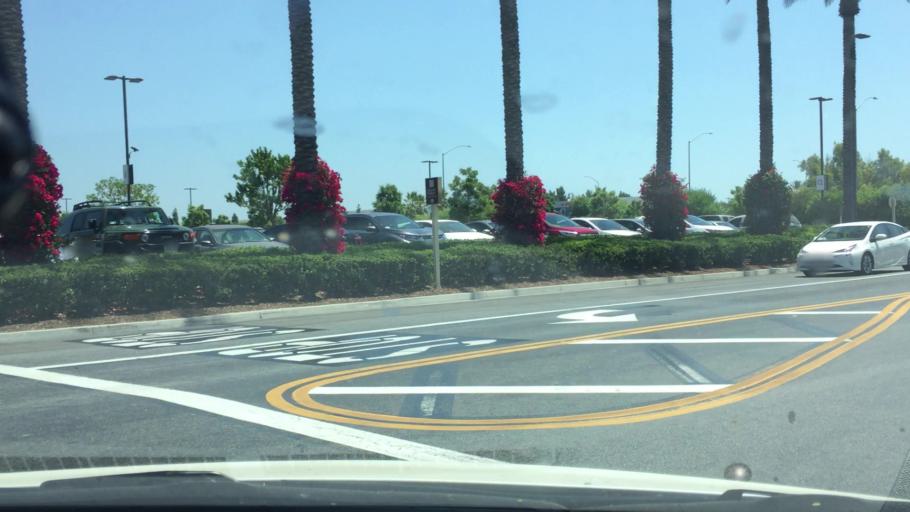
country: US
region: California
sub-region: Orange County
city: Laguna Woods
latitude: 33.6485
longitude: -117.7437
